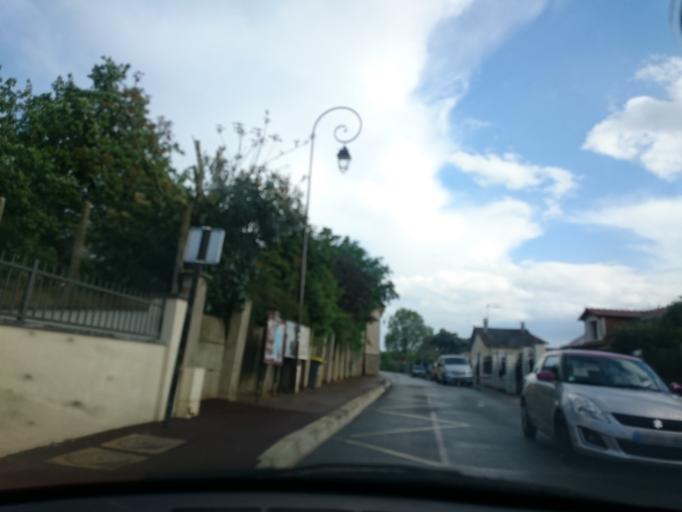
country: FR
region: Ile-de-France
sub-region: Departement de l'Essonne
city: Etiolles
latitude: 48.6317
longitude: 2.4722
